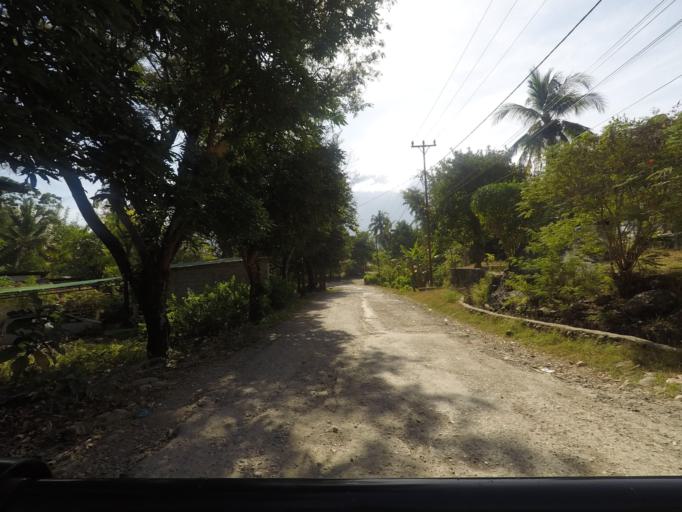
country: TL
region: Bobonaro
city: Maliana
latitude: -8.9941
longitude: 125.2247
